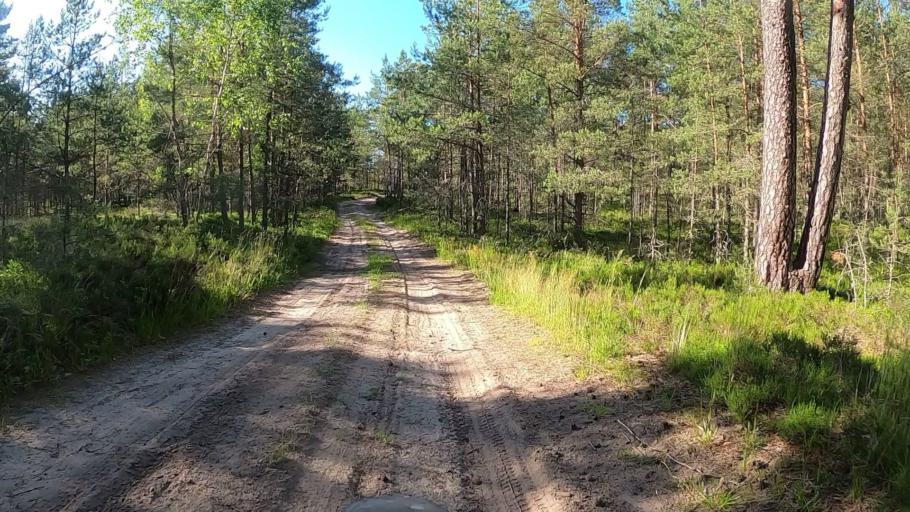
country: LV
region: Carnikava
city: Carnikava
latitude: 57.1003
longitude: 24.2356
